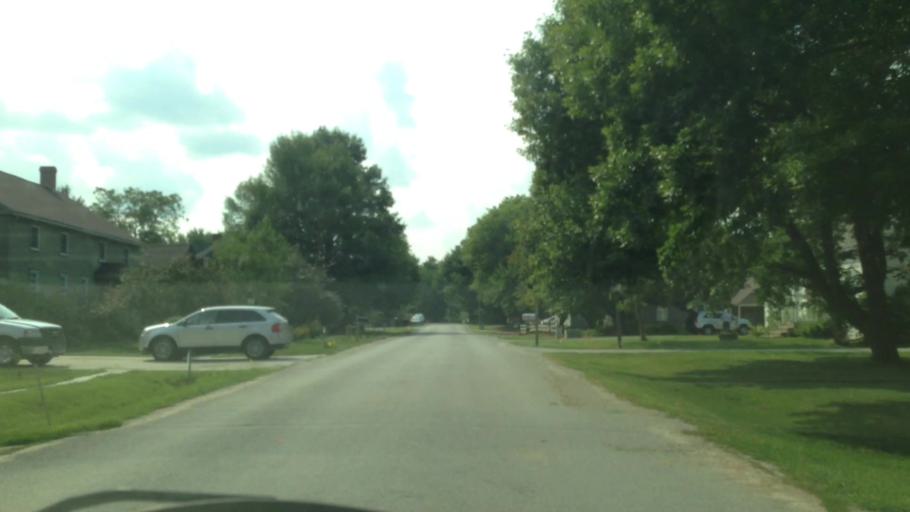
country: US
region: Iowa
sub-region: Benton County
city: Walford
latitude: 41.7966
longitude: -91.9008
